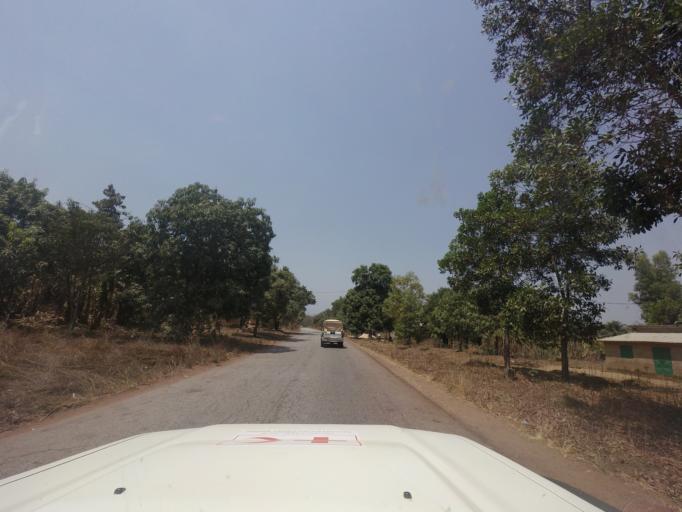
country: GN
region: Kindia
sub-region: Coyah
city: Coyah
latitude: 9.8400
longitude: -13.0993
